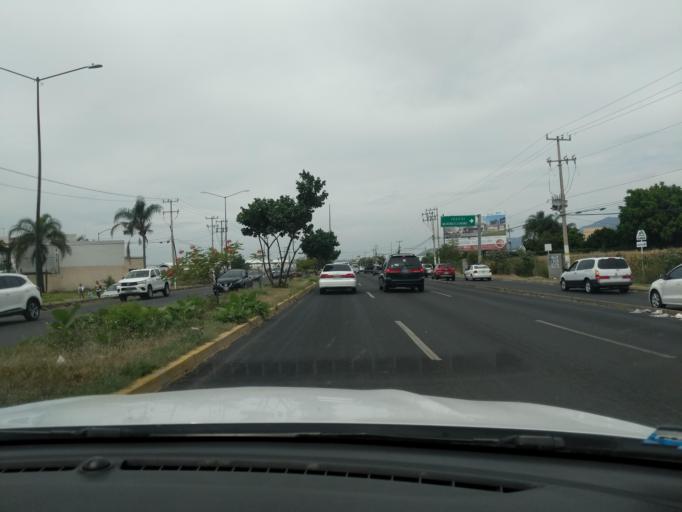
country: MX
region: Jalisco
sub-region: Zapopan
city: La Cuchilla (Extramuros de Tesistan)
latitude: 20.7805
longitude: -103.4615
